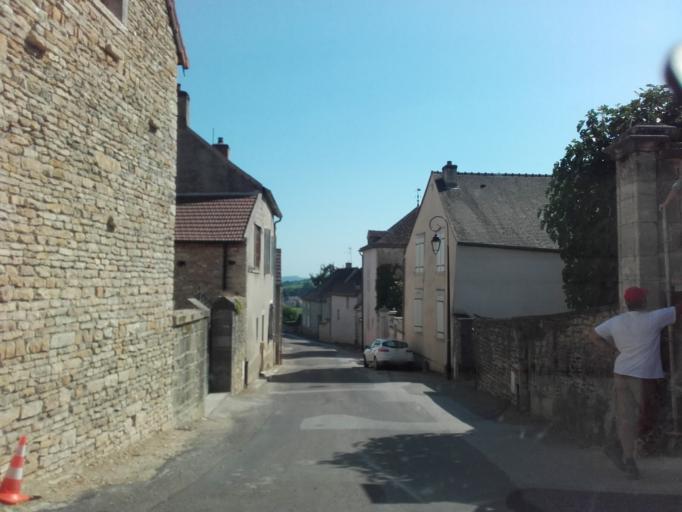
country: FR
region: Bourgogne
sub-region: Departement de la Cote-d'Or
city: Meursault
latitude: 46.9920
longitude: 4.7668
